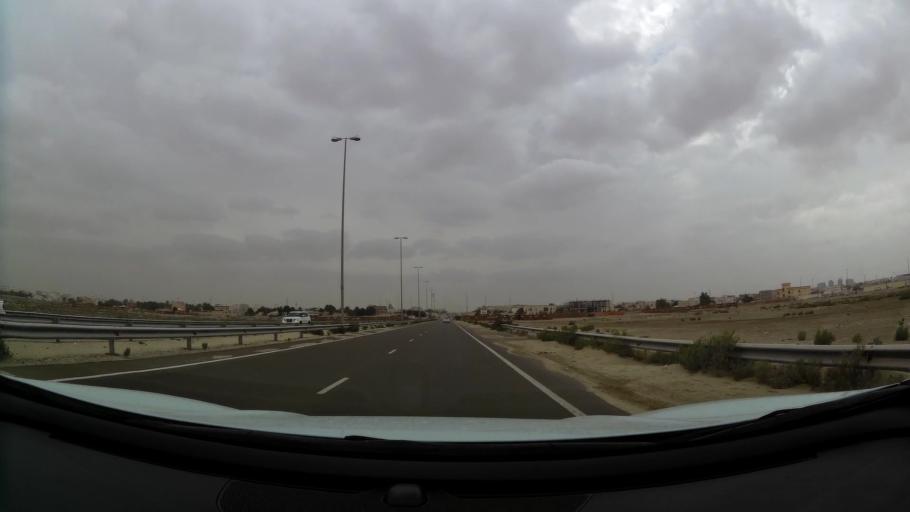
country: AE
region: Abu Dhabi
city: Abu Dhabi
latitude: 24.3254
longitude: 54.6434
